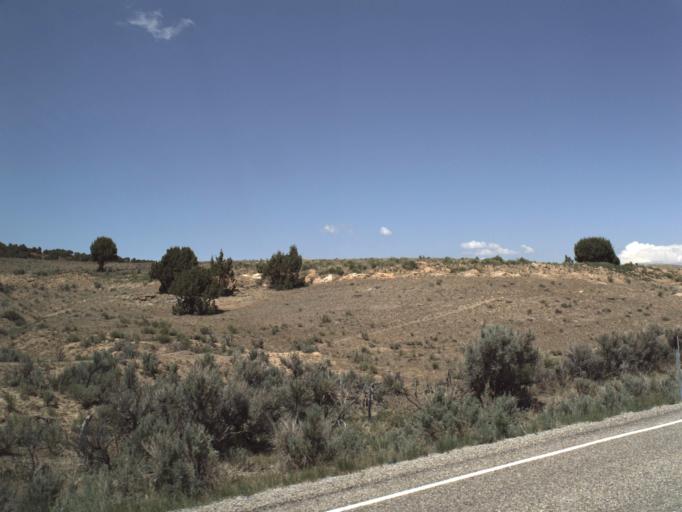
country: US
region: Utah
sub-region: Rich County
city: Randolph
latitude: 41.5147
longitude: -111.2141
